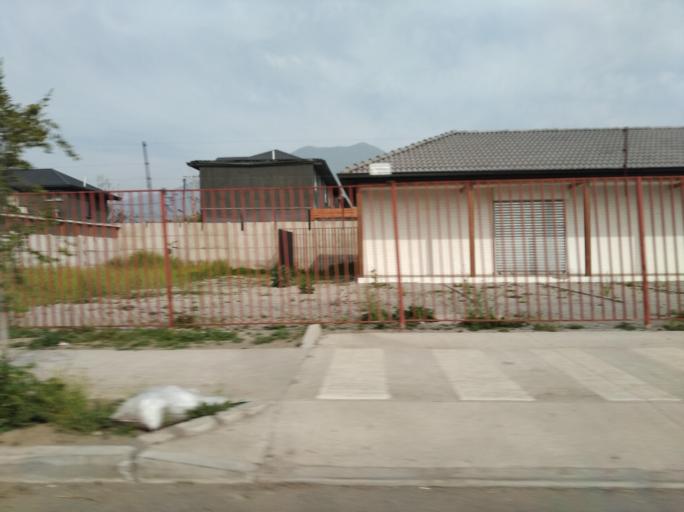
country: CL
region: Santiago Metropolitan
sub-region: Provincia de Chacabuco
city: Lampa
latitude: -33.2999
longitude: -70.8786
